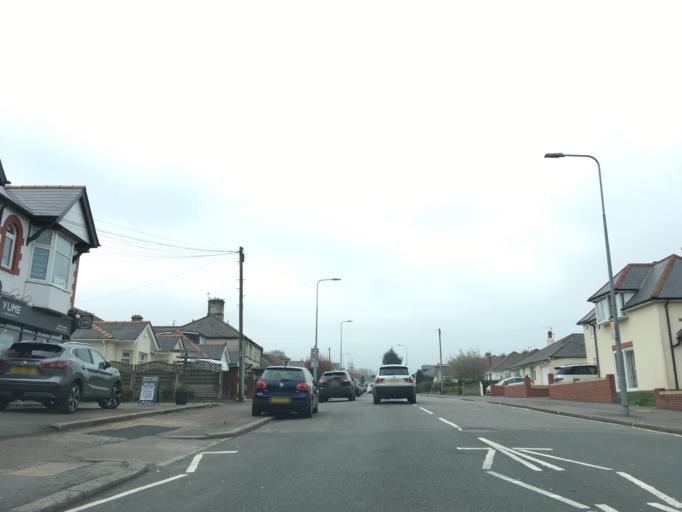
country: GB
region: Wales
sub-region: Cardiff
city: Cardiff
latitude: 51.5203
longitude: -3.1791
